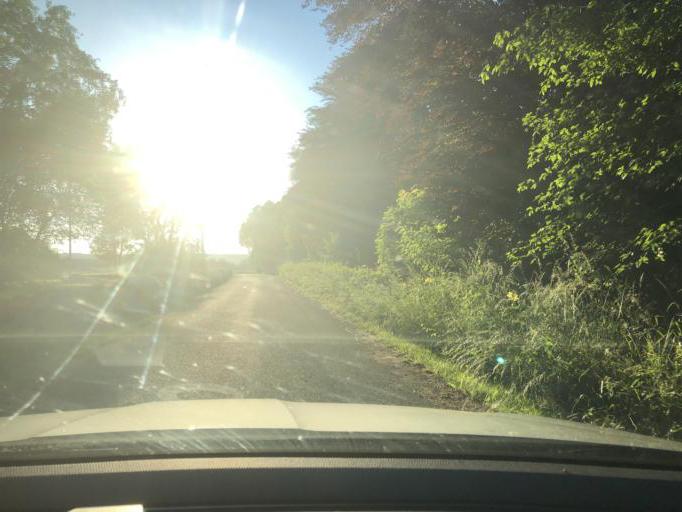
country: SE
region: Blekinge
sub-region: Karlshamns Kommun
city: Morrum
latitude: 56.1356
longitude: 14.6649
